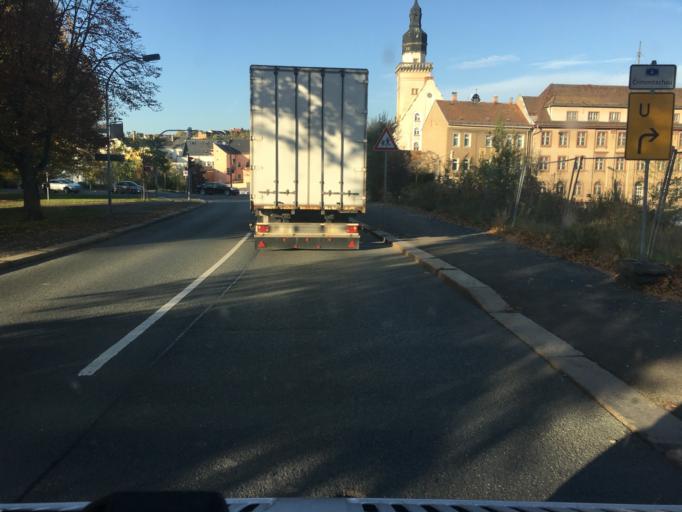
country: DE
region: Saxony
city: Werdau
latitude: 50.7361
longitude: 12.3792
